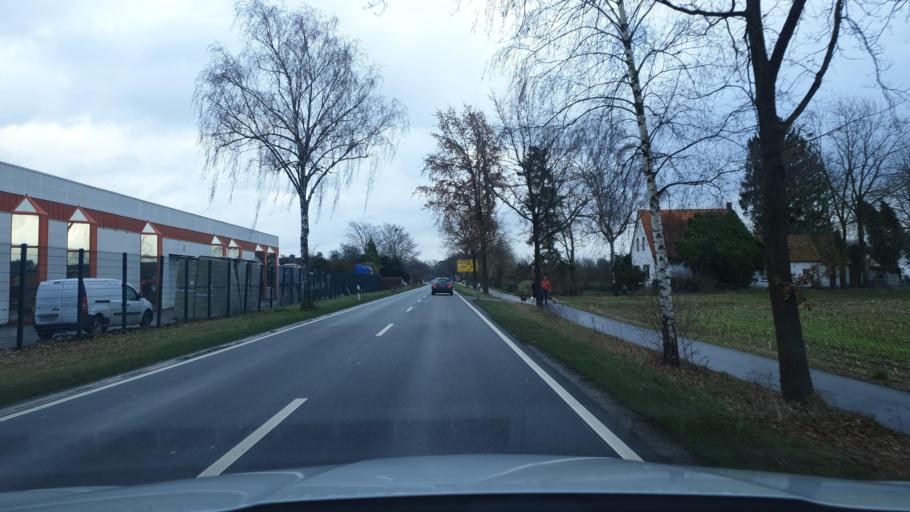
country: DE
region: North Rhine-Westphalia
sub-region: Regierungsbezirk Detmold
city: Verl
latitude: 51.8945
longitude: 8.4669
